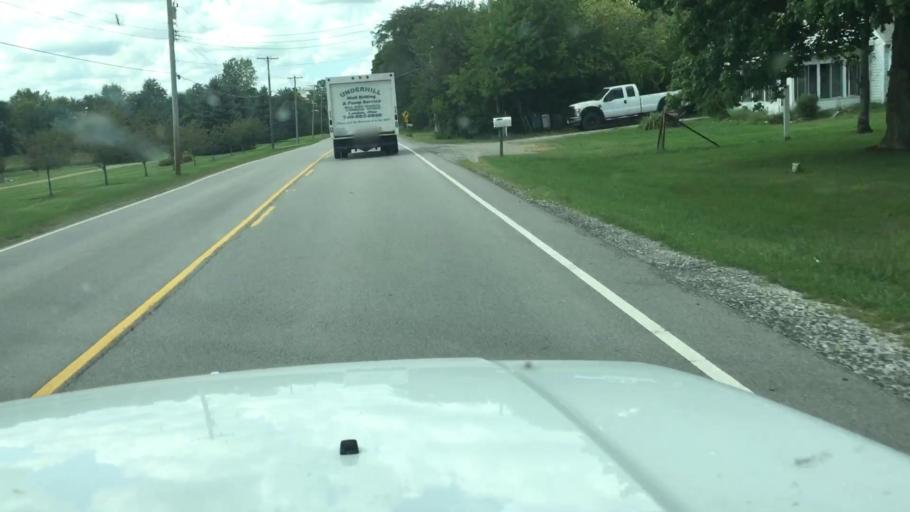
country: US
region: Ohio
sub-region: Madison County
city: London
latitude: 39.8753
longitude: -83.4294
